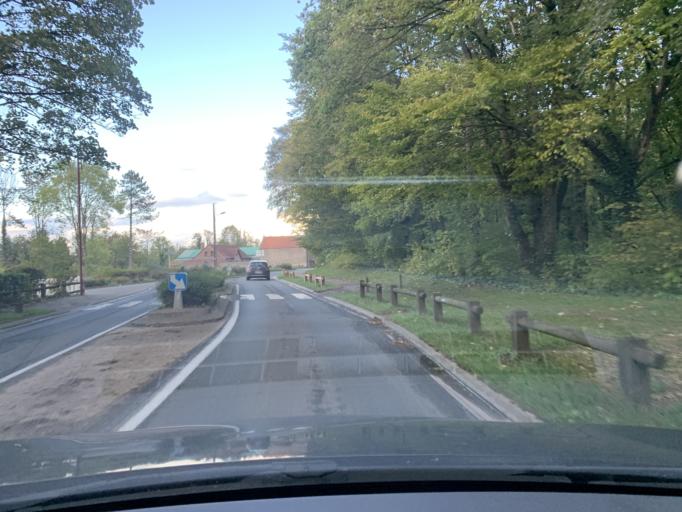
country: FR
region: Nord-Pas-de-Calais
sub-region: Departement du Nord
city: Proville
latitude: 50.1617
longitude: 3.2131
